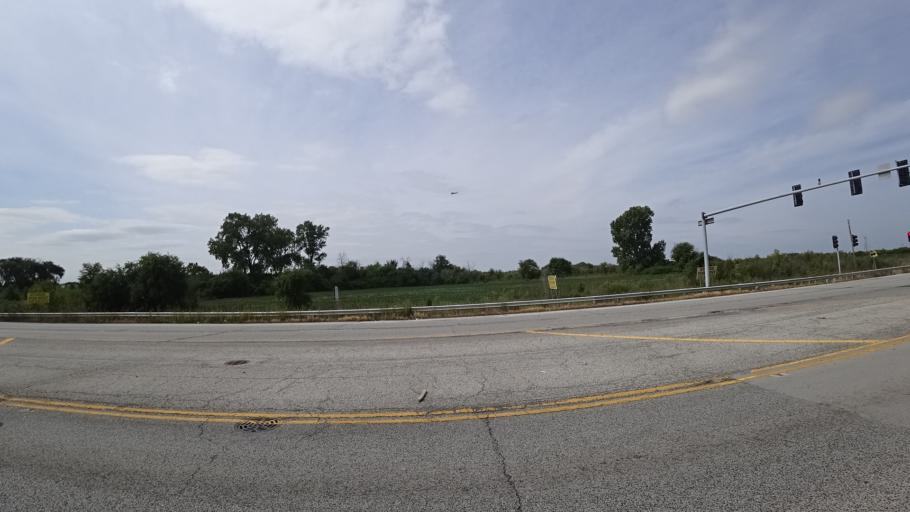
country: US
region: Illinois
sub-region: Will County
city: Frankfort Square
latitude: 41.5396
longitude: -87.7906
